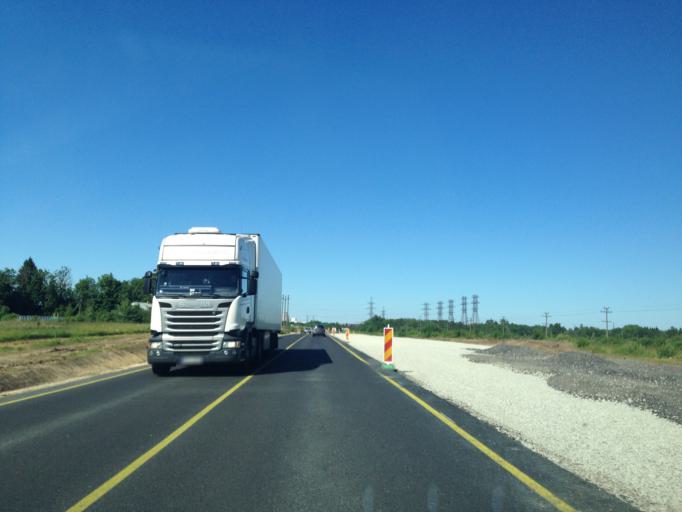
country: EE
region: Harju
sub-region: Joelaehtme vald
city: Loo
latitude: 59.4181
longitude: 24.9200
